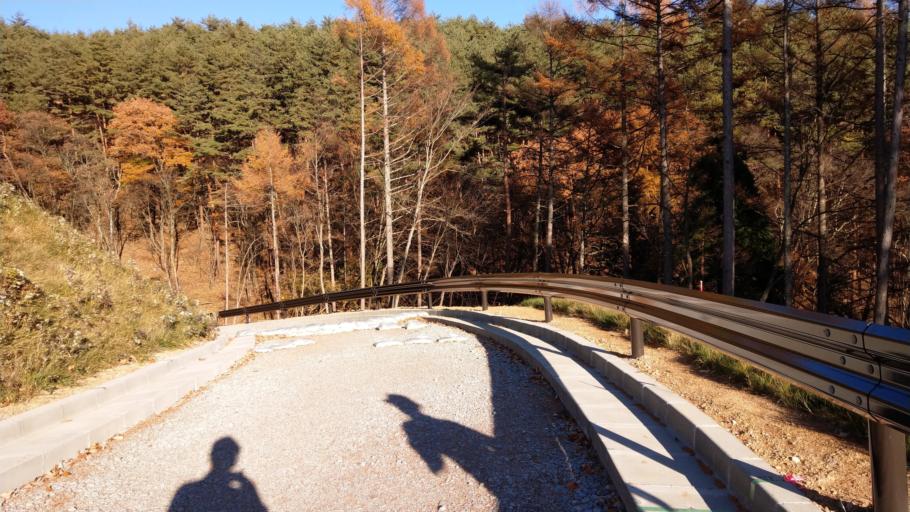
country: JP
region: Nagano
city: Komoro
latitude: 36.3634
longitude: 138.4317
